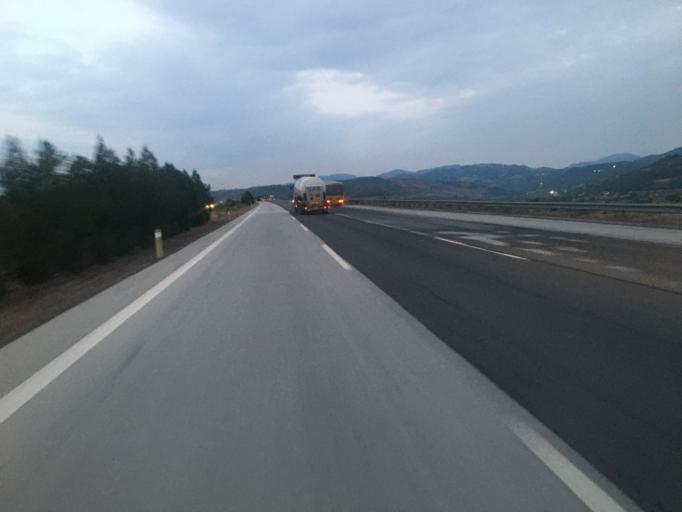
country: TR
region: Osmaniye
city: Kaypak
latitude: 37.1566
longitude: 36.3533
